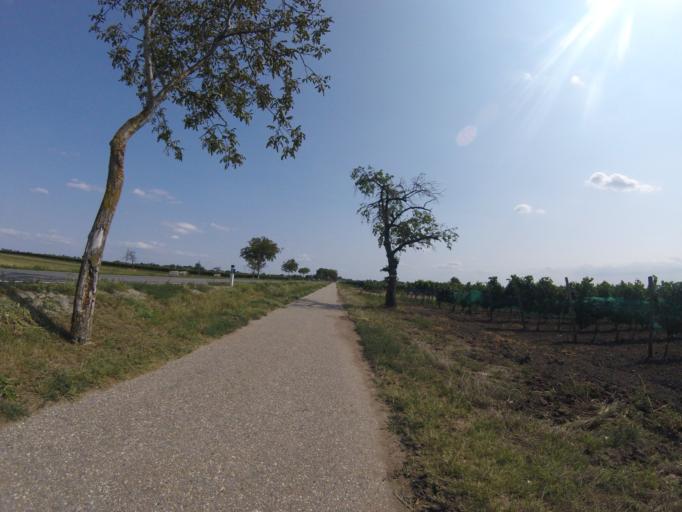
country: AT
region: Burgenland
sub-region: Politischer Bezirk Neusiedl am See
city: Apetlon
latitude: 47.7528
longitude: 16.8176
